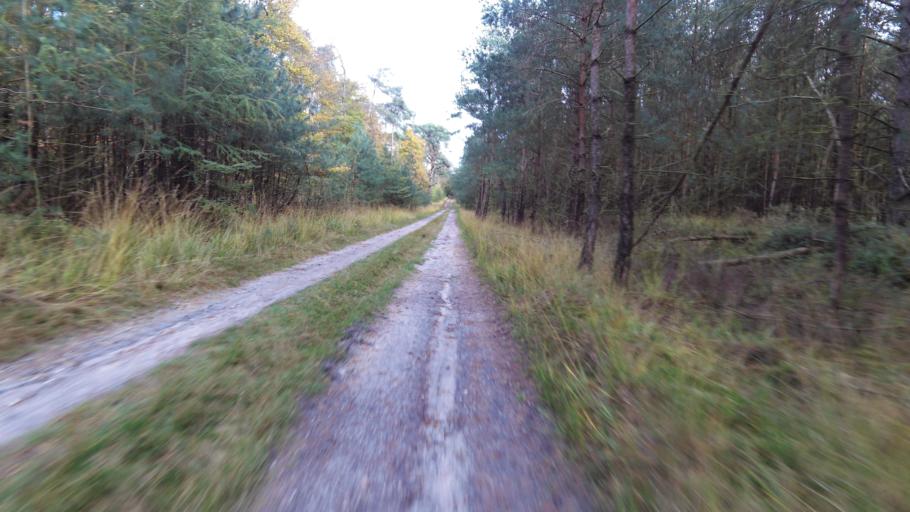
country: NL
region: Gelderland
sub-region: Gemeente Apeldoorn
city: Uddel
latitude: 52.3140
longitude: 5.8579
